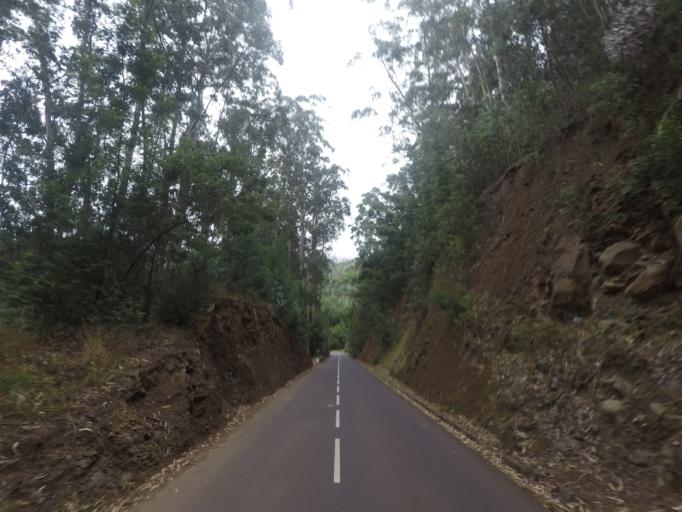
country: PT
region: Madeira
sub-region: Funchal
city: Nossa Senhora do Monte
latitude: 32.6692
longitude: -16.8788
